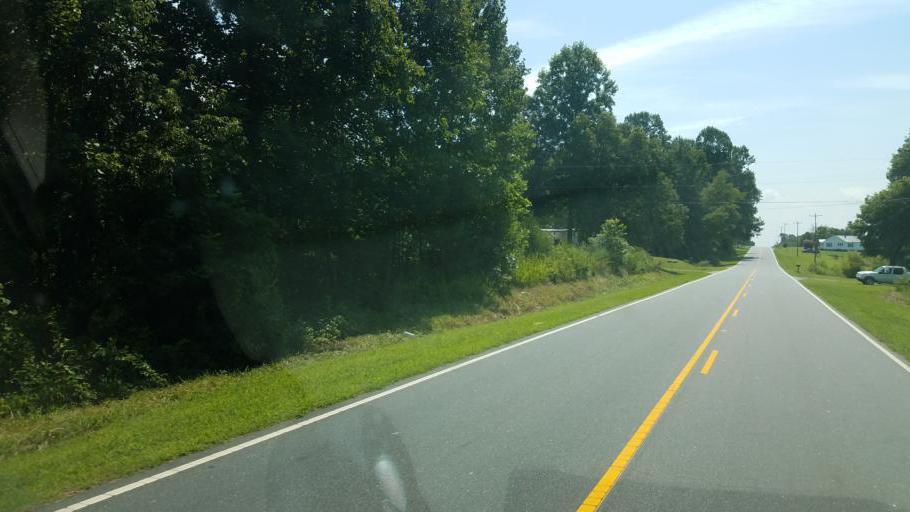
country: US
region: North Carolina
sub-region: Gaston County
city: Cherryville
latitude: 35.5201
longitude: -81.4821
